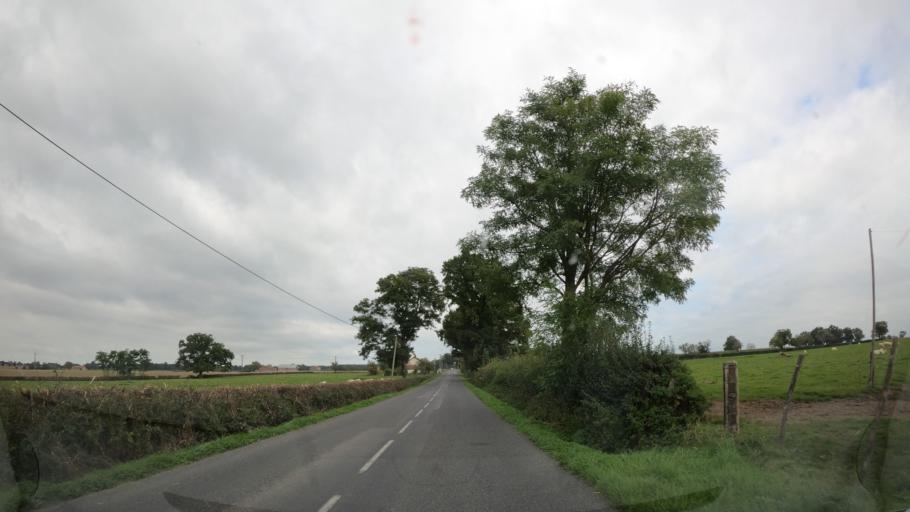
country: FR
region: Auvergne
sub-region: Departement de l'Allier
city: Saint-Gerand-le-Puy
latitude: 46.2678
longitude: 3.5410
